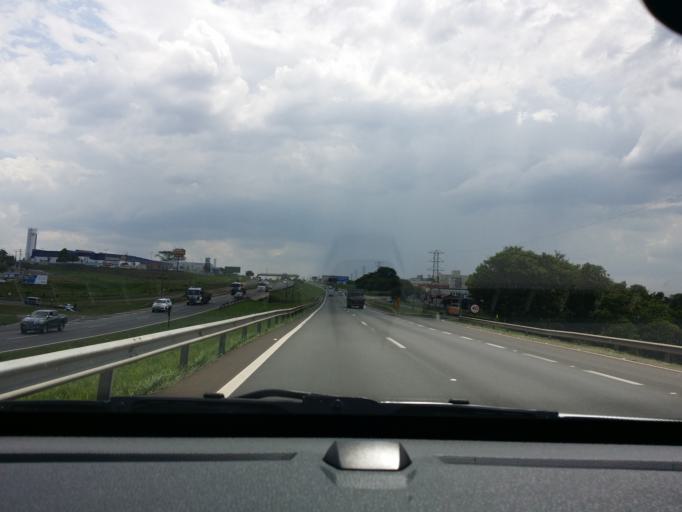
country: BR
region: Sao Paulo
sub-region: Rio Claro
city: Rio Claro
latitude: -22.4209
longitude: -47.5770
